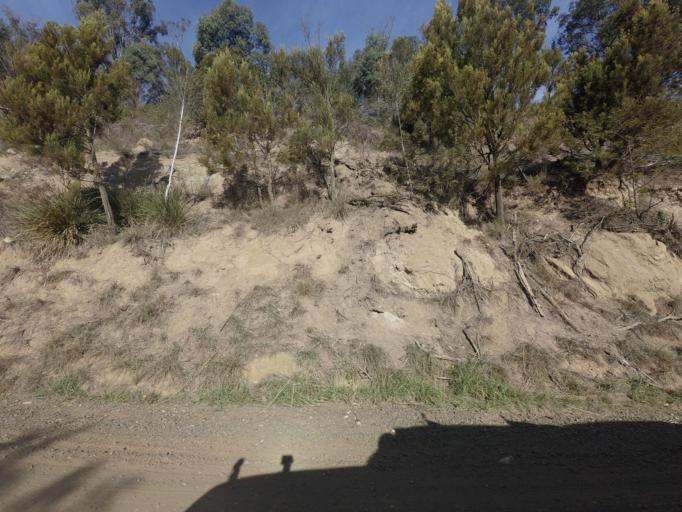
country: AU
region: Tasmania
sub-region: Sorell
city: Sorell
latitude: -42.5011
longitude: 147.4321
